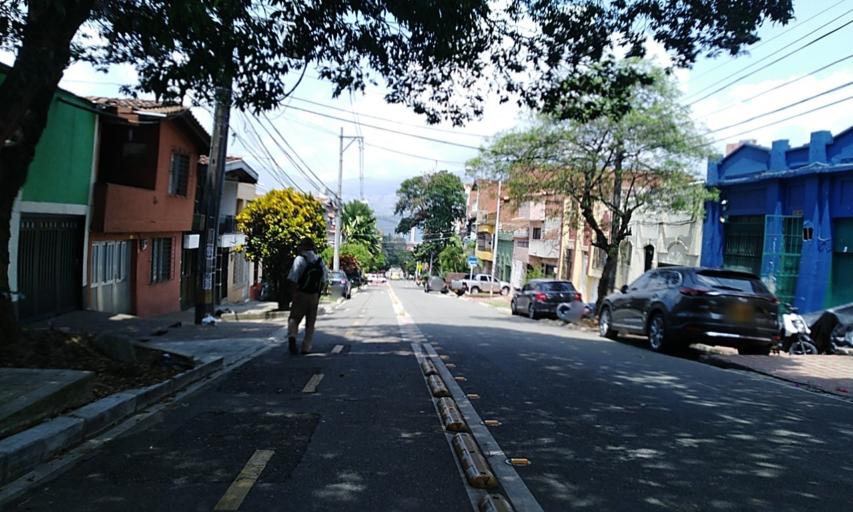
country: CO
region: Antioquia
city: Medellin
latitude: 6.2467
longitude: -75.5532
